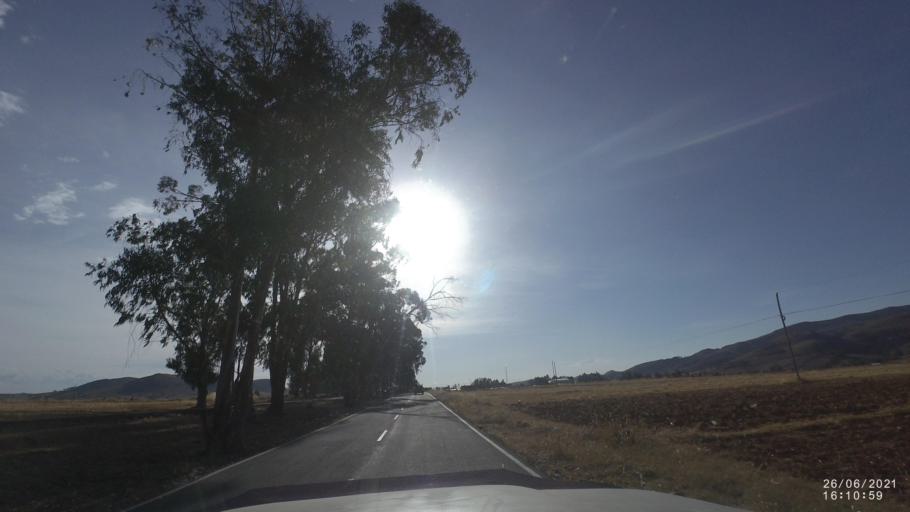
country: BO
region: Cochabamba
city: Arani
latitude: -17.8077
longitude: -65.7940
